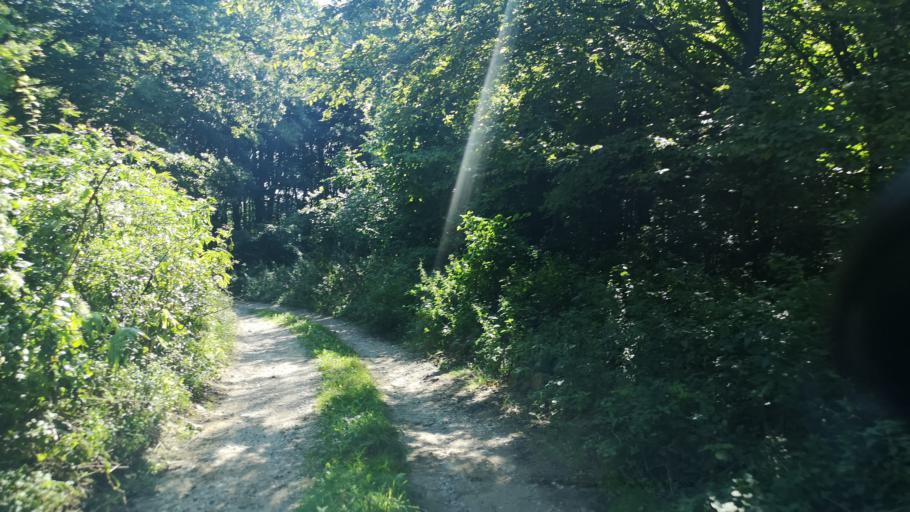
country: SK
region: Trnavsky
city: Smolenice
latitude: 48.5739
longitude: 17.4368
